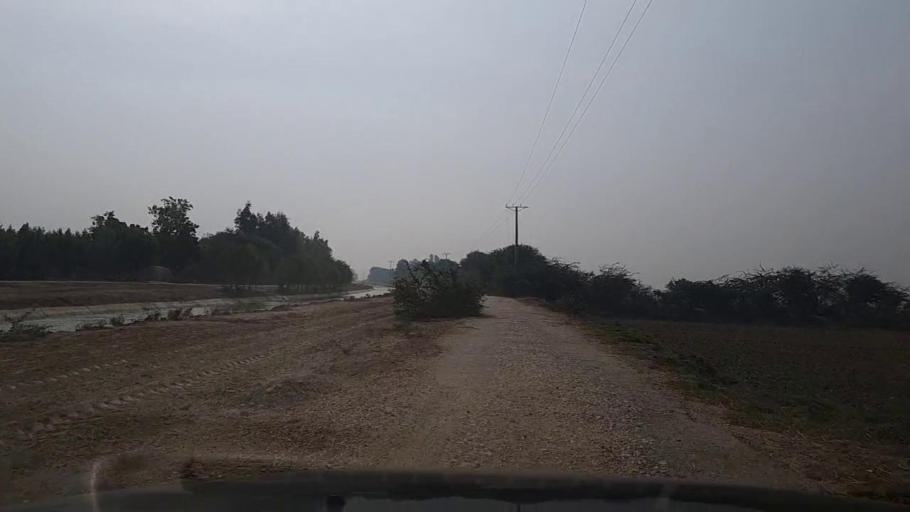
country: PK
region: Sindh
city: Mirpur Sakro
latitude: 24.5429
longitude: 67.8125
